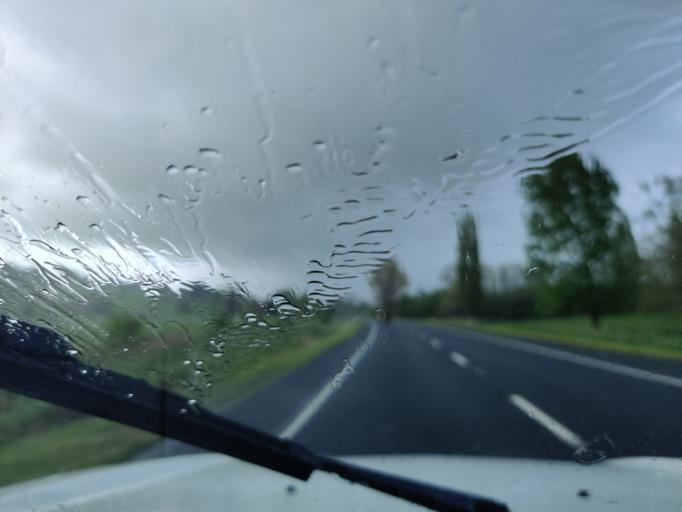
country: NZ
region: Waikato
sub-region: Matamata-Piako District
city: Matamata
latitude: -37.9760
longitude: 175.6966
